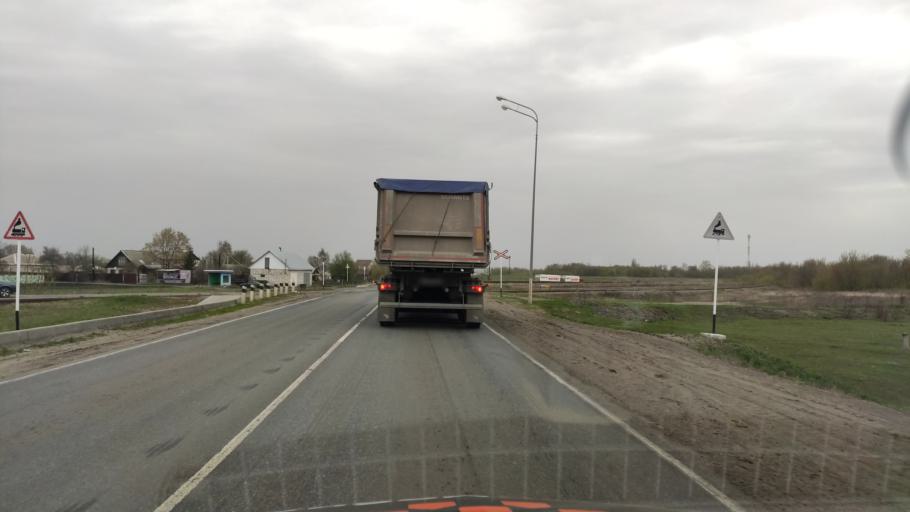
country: RU
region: Kursk
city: Gorshechnoye
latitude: 51.5268
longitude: 38.0230
